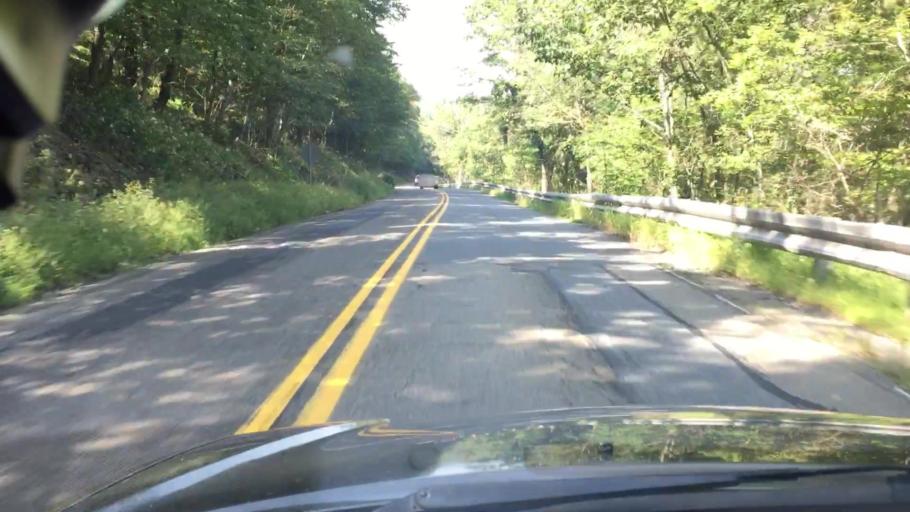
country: US
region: Pennsylvania
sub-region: Luzerne County
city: Harleigh
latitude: 41.0003
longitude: -75.9855
